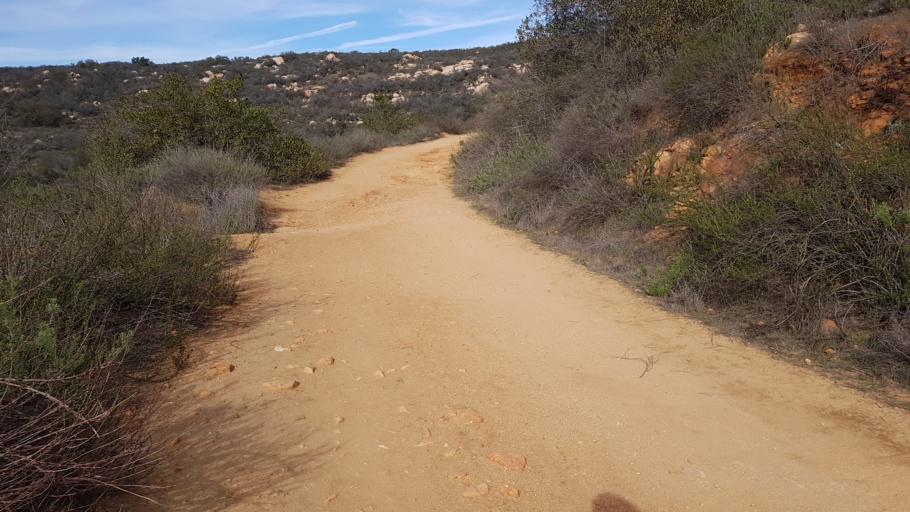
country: US
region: California
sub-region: San Diego County
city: Valley Center
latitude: 33.1748
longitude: -117.0356
